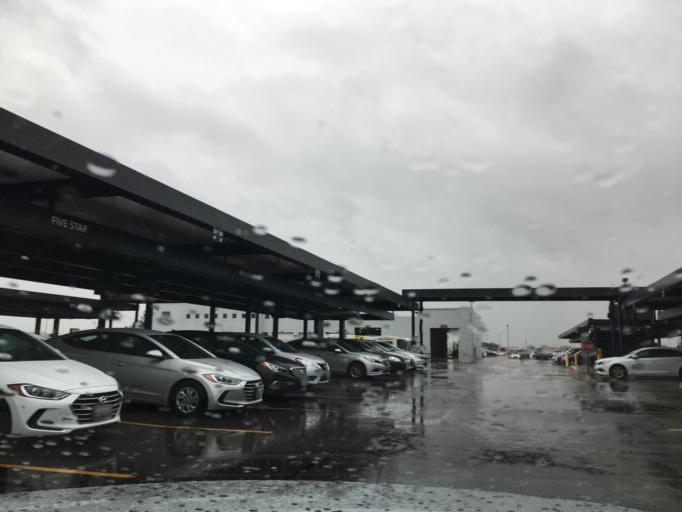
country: US
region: Michigan
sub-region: Wayne County
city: Inkster
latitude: 42.2374
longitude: -83.3342
